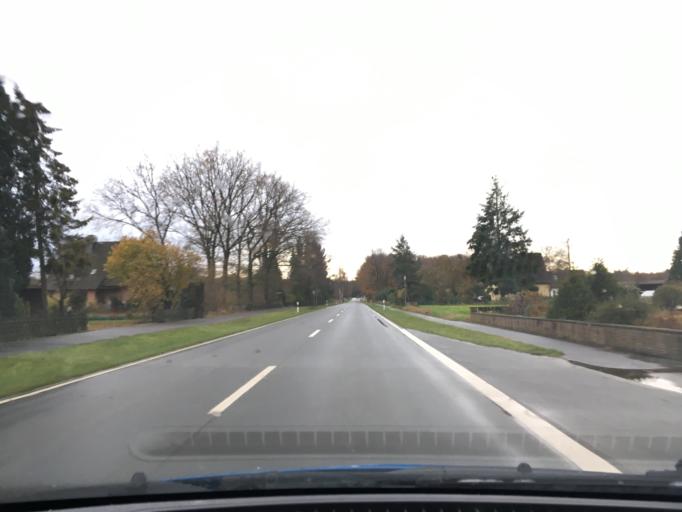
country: DE
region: Lower Saxony
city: Wriedel
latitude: 52.9929
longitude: 10.2569
